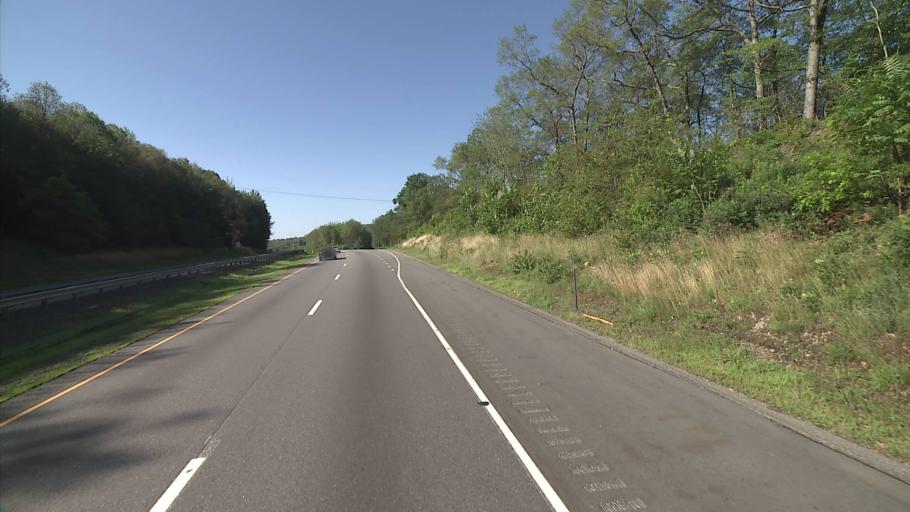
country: US
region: Connecticut
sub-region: New London County
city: Oxoboxo River
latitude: 41.4485
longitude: -72.1178
